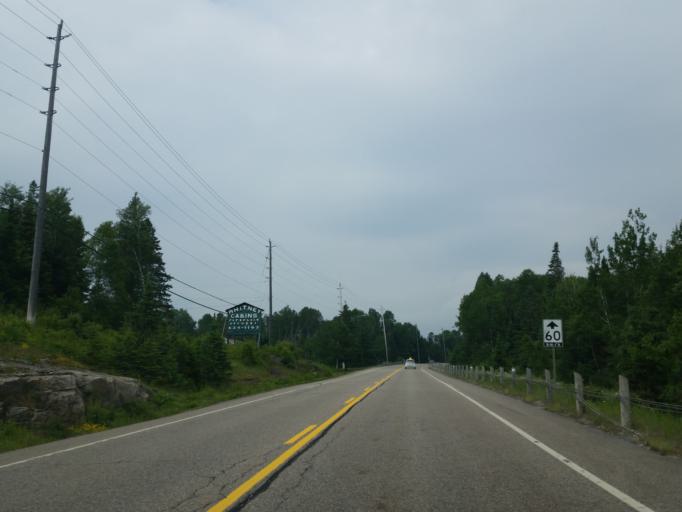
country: CA
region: Ontario
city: Bancroft
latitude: 45.4892
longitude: -78.2247
